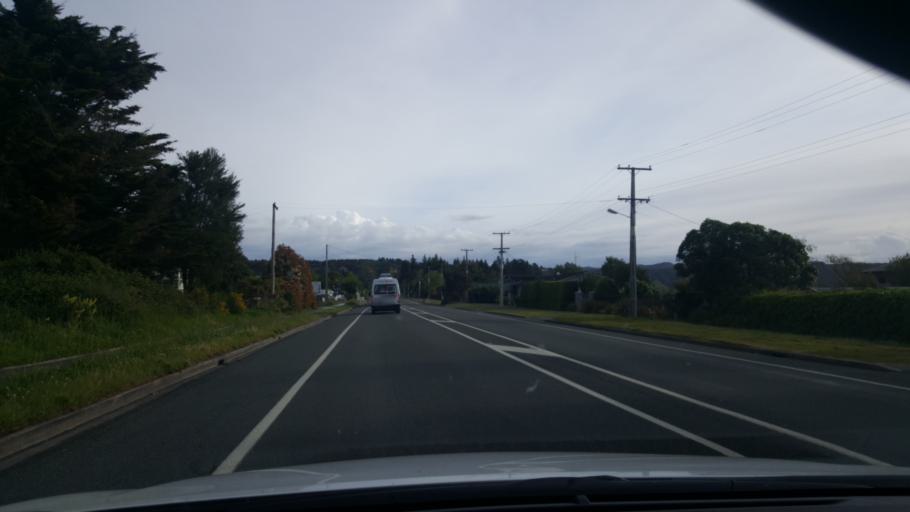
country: NZ
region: Waikato
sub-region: Taupo District
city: Taupo
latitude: -38.7893
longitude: 176.0764
